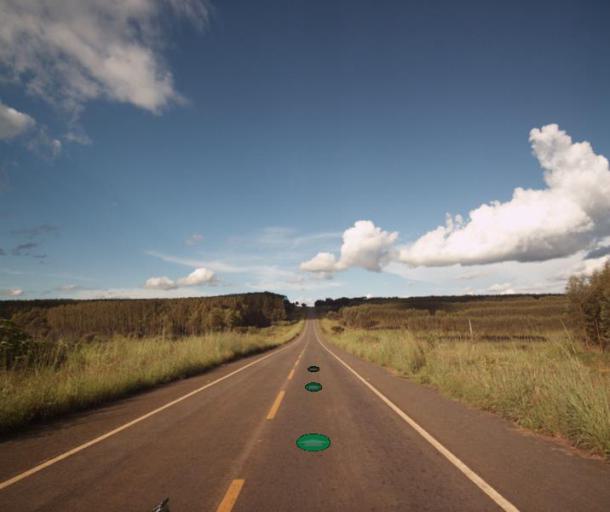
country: BR
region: Goias
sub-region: Itaberai
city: Itaberai
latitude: -15.9884
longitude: -49.7162
